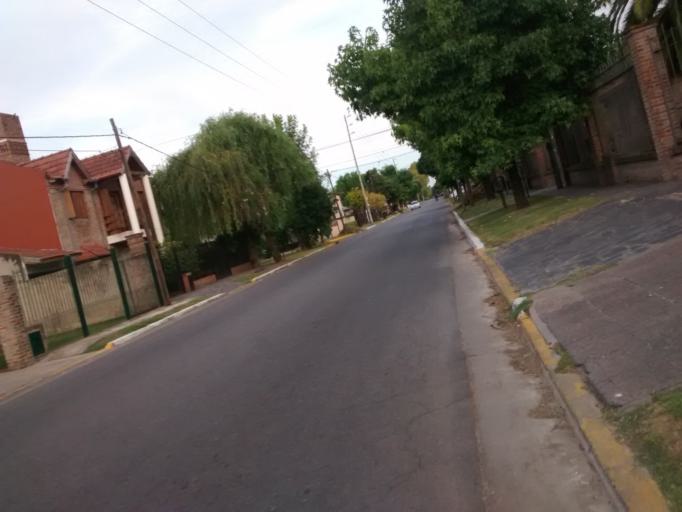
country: AR
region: Buenos Aires
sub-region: Partido de La Plata
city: La Plata
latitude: -34.8928
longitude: -58.0334
